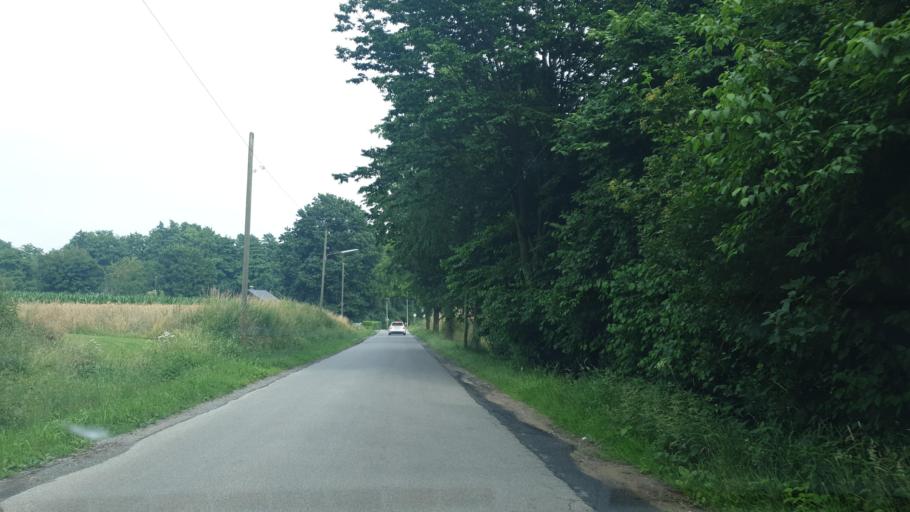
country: DE
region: North Rhine-Westphalia
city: Bad Oeynhausen
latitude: 52.2417
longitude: 8.7594
